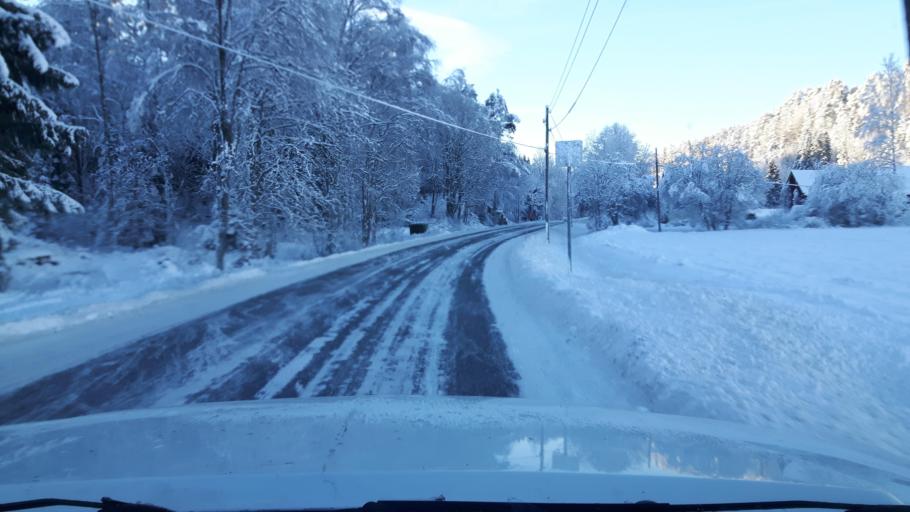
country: SE
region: Halland
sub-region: Kungsbacka Kommun
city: Fjaeras kyrkby
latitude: 57.5532
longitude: 12.1991
